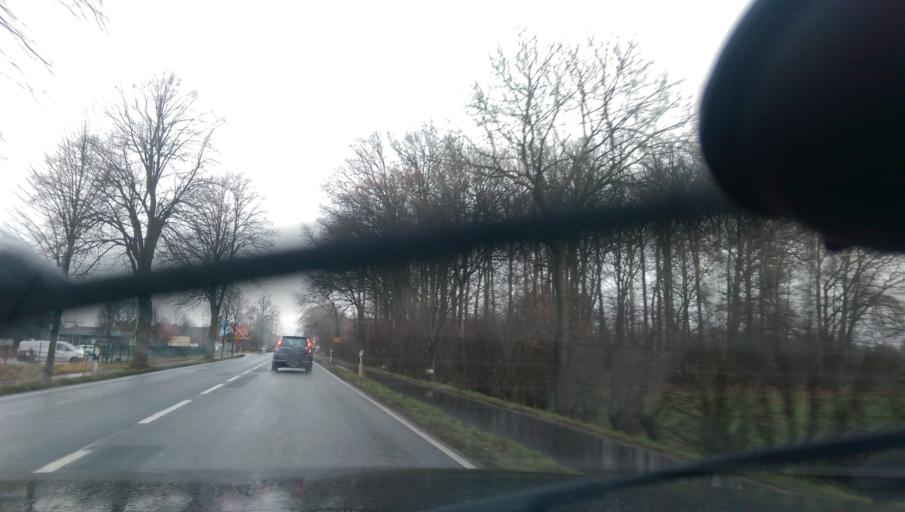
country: DE
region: Lower Saxony
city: Verden
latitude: 52.9110
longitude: 9.2171
